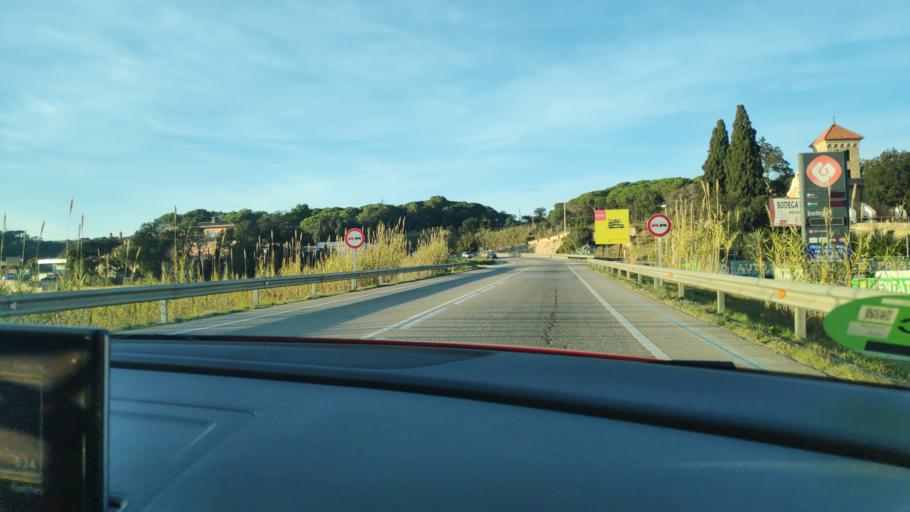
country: ES
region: Catalonia
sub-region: Provincia de Girona
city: Lloret de Mar
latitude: 41.7165
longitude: 2.8296
